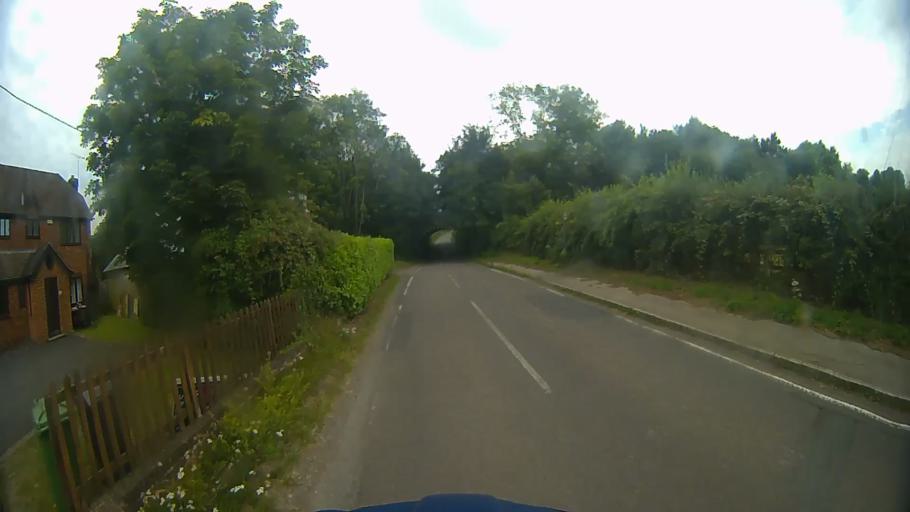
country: GB
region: England
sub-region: Hampshire
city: Kingsley
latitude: 51.1801
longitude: -0.8732
